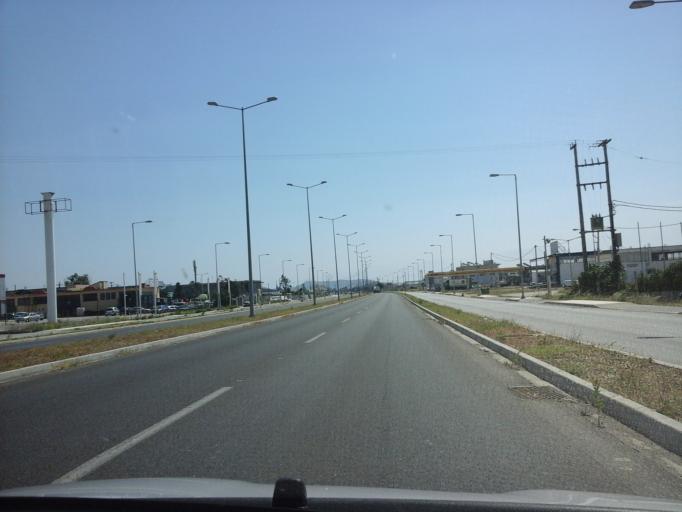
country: GR
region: East Macedonia and Thrace
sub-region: Nomos Evrou
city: Alexandroupoli
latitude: 40.8542
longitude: 25.9188
